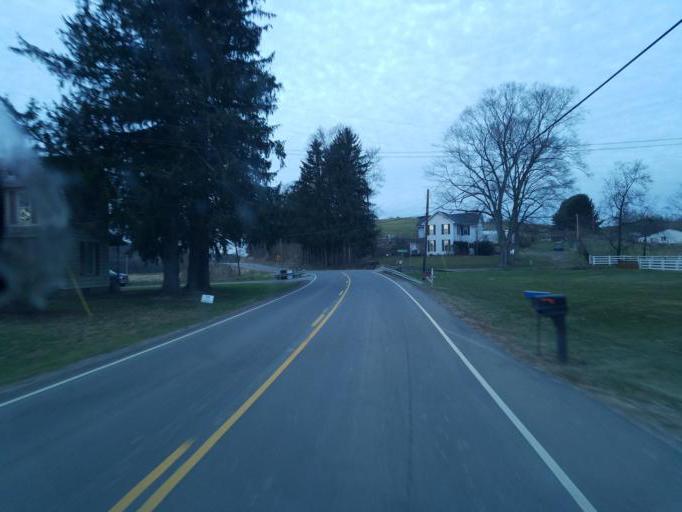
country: US
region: Ohio
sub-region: Muskingum County
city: Dresden
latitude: 40.2001
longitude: -82.0483
